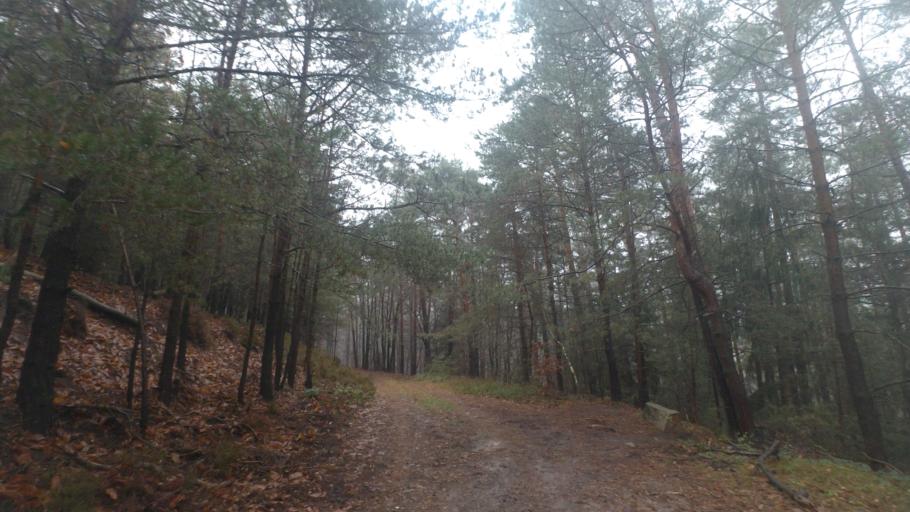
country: DE
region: Rheinland-Pfalz
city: Lindenberg
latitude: 49.3931
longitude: 8.1355
